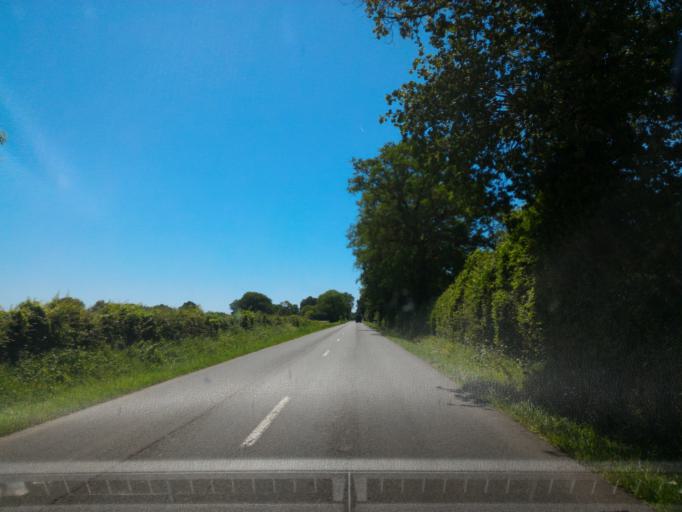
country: FR
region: Poitou-Charentes
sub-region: Departement de la Vienne
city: Availles-Limouzine
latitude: 46.1435
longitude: 0.7148
